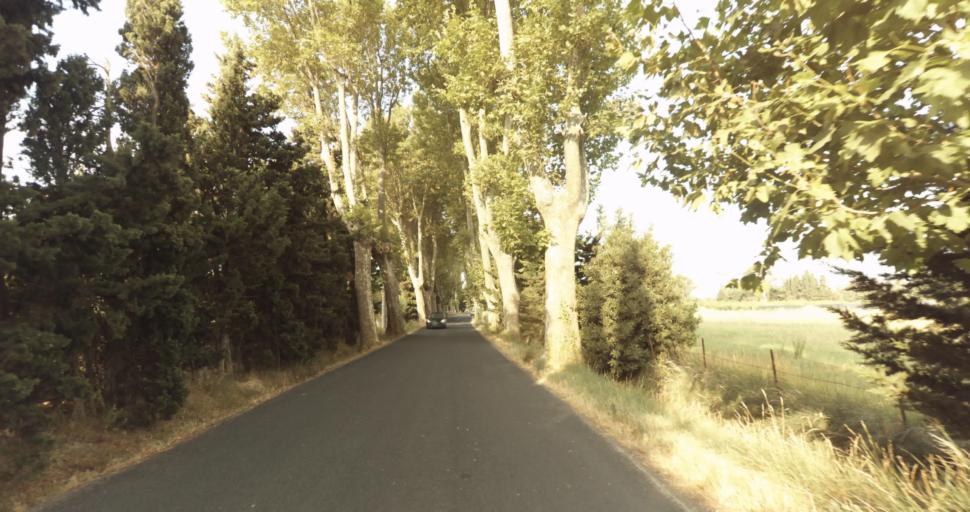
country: FR
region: Languedoc-Roussillon
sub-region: Departement des Pyrenees-Orientales
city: Theza
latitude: 42.6360
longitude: 2.9461
